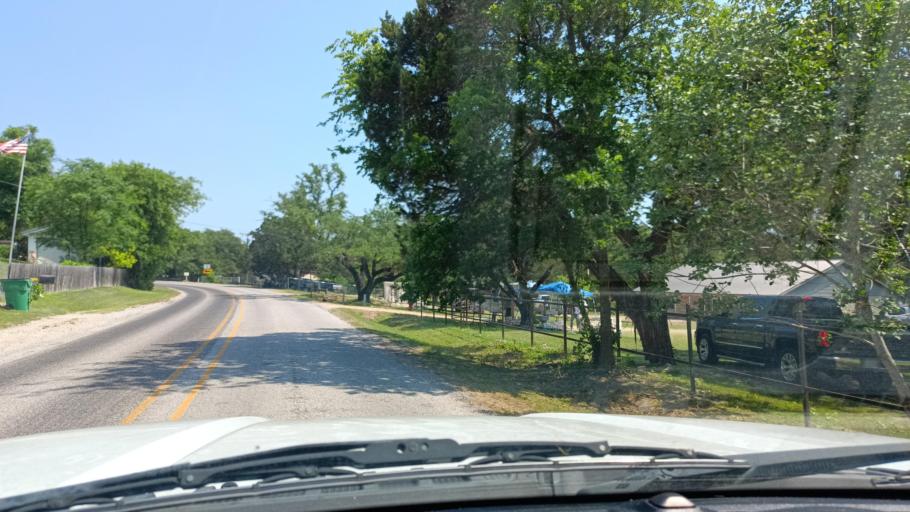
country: US
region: Texas
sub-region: Bell County
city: Morgans Point Resort
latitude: 31.1145
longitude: -97.5331
